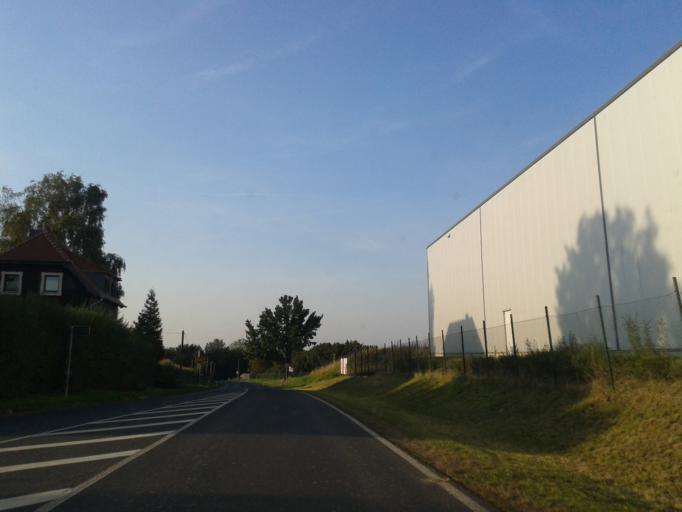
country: DE
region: Saxony
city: Klipphausen
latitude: 51.0978
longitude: 13.4959
